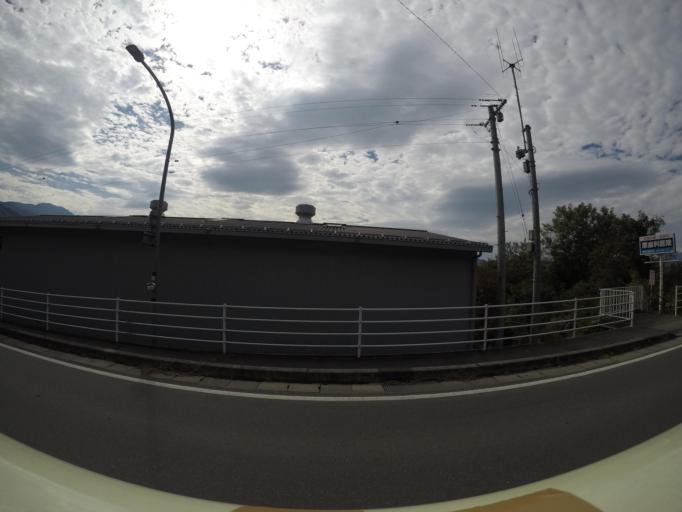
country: JP
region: Nagano
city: Ina
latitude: 35.8380
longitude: 138.0526
